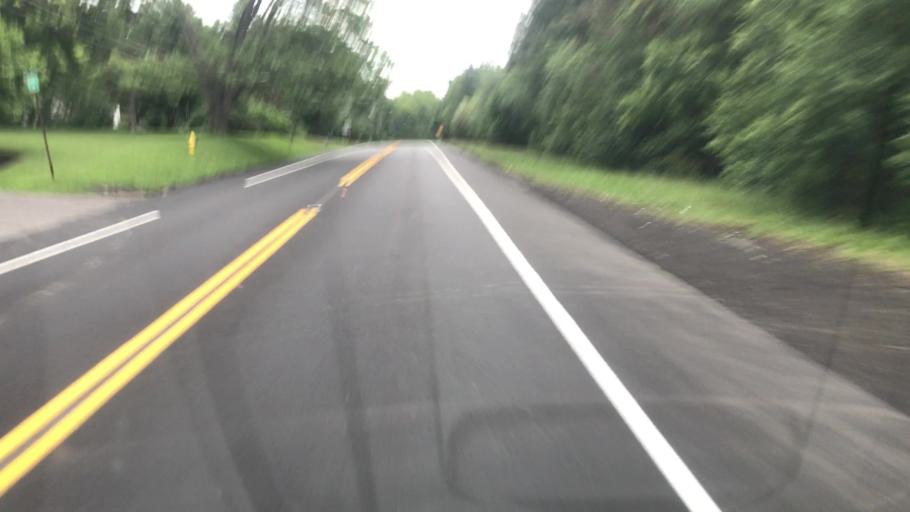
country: US
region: New York
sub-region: Cayuga County
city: Melrose Park
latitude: 42.8985
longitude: -76.5242
